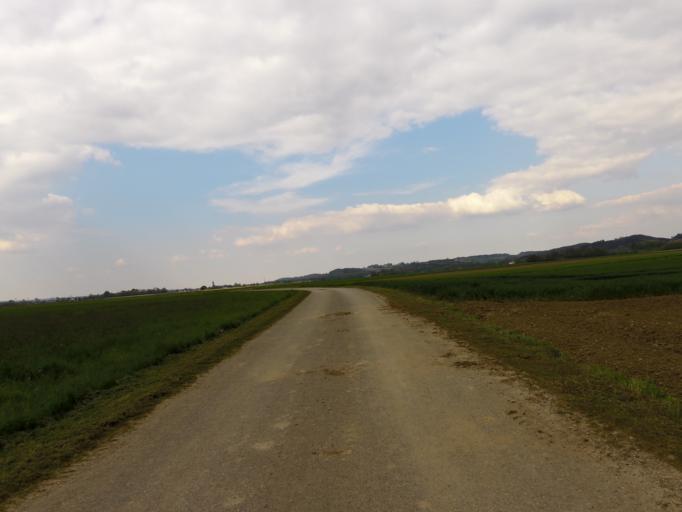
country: DE
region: Bavaria
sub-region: Upper Bavaria
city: Langenpreising
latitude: 48.4065
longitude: 11.9583
